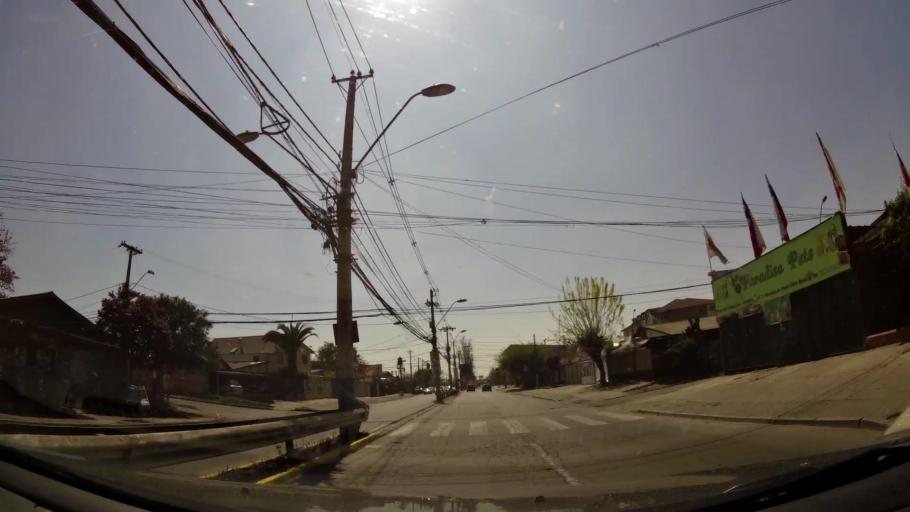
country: CL
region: Santiago Metropolitan
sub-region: Provincia de Santiago
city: Lo Prado
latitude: -33.3641
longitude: -70.7299
